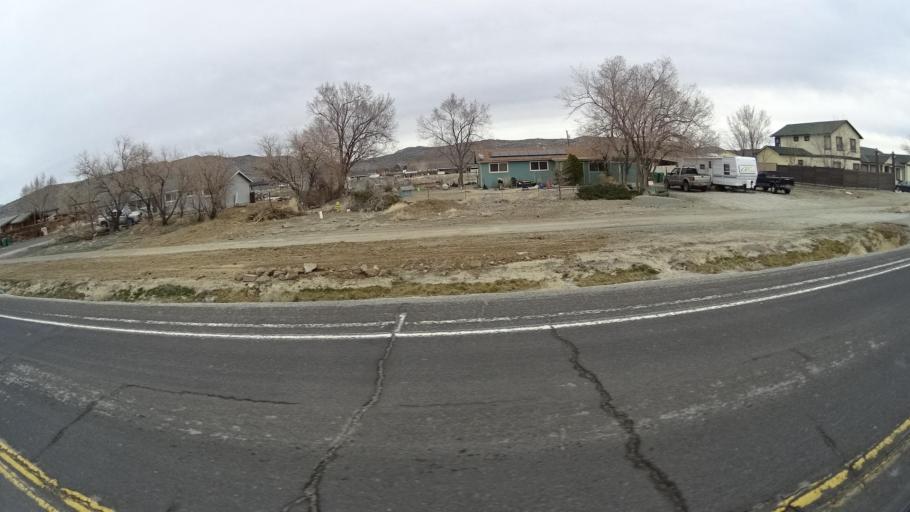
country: US
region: Nevada
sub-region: Washoe County
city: Lemmon Valley
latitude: 39.6723
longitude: -119.8364
